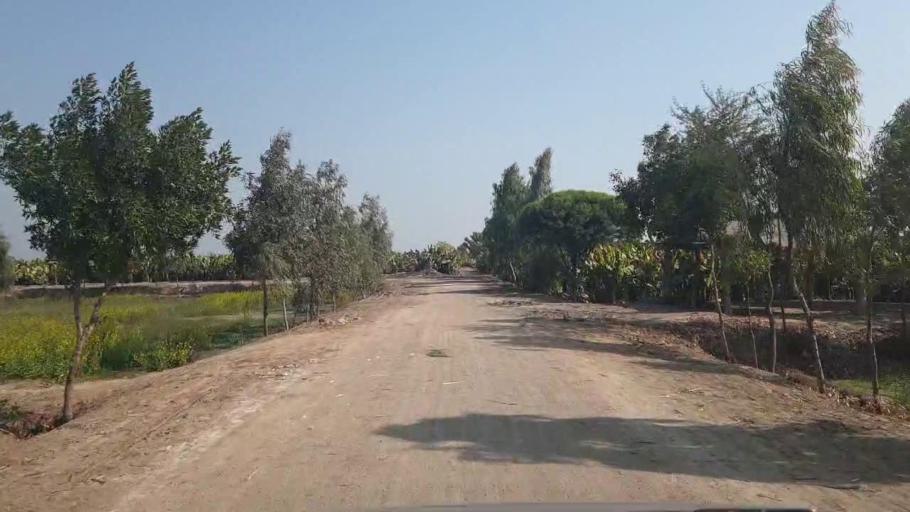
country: PK
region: Sindh
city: Tando Adam
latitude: 25.7985
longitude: 68.6291
